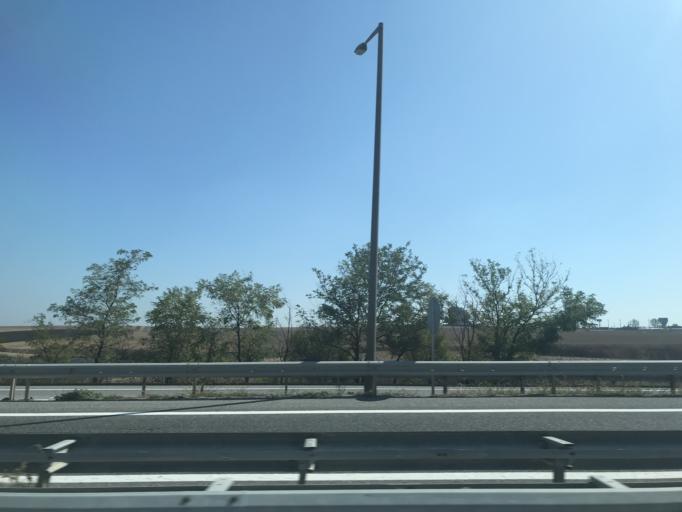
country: TR
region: Kirklareli
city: Luleburgaz
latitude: 41.3936
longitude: 27.3859
